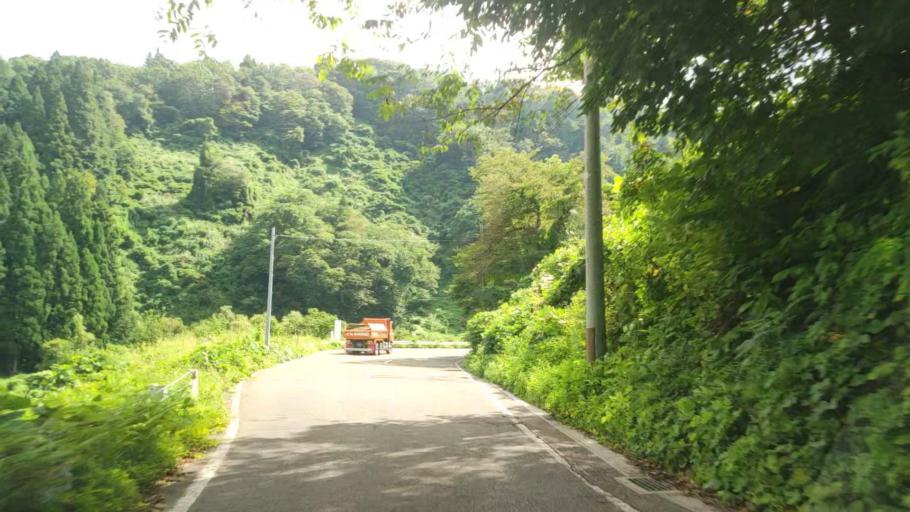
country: JP
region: Niigata
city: Arai
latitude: 36.9450
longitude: 138.2908
